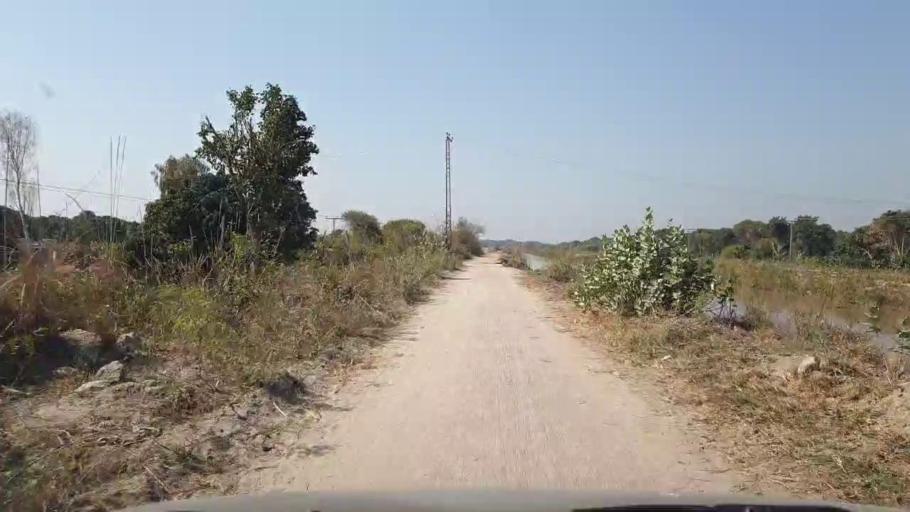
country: PK
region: Sindh
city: Tando Jam
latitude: 25.4478
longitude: 68.6174
